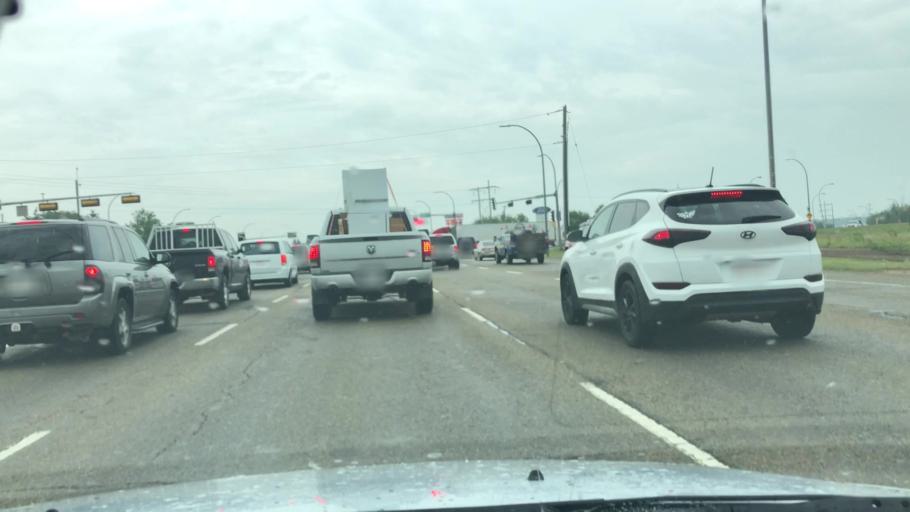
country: CA
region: Alberta
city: St. Albert
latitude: 53.6122
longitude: -113.5924
